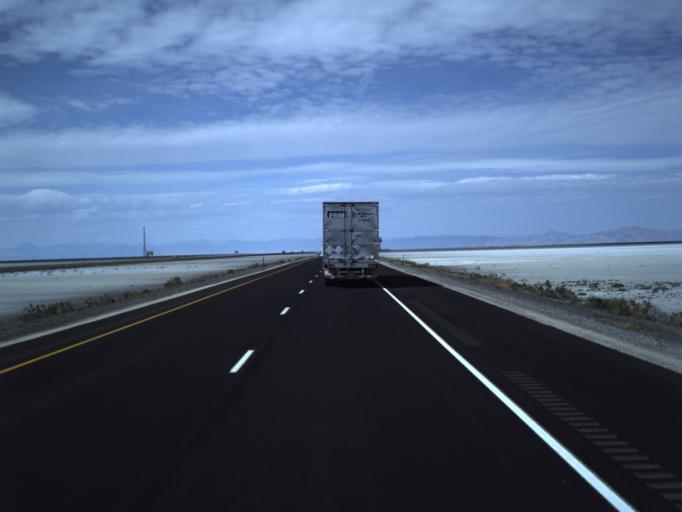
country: US
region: Utah
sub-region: Tooele County
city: Wendover
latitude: 40.7326
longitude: -113.5329
